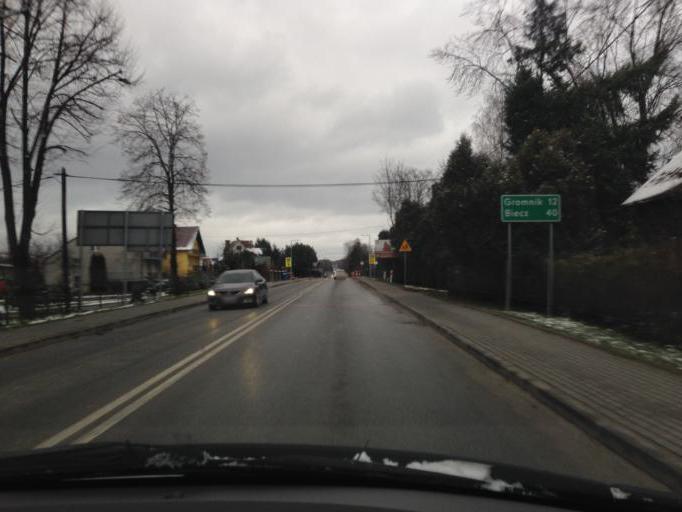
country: PL
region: Lesser Poland Voivodeship
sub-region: Powiat tarnowski
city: Zakliczyn
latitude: 49.8559
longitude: 20.8151
